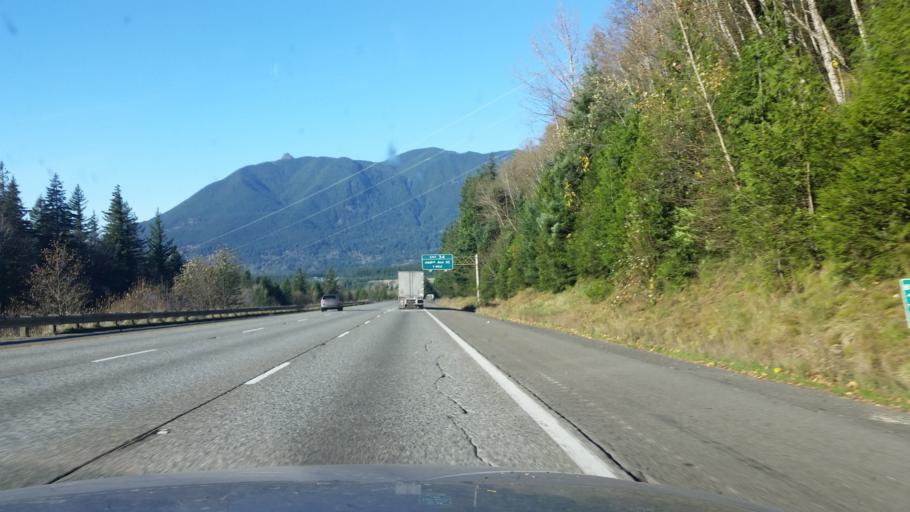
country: US
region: Washington
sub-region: King County
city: Tanner
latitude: 47.4516
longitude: -121.7004
